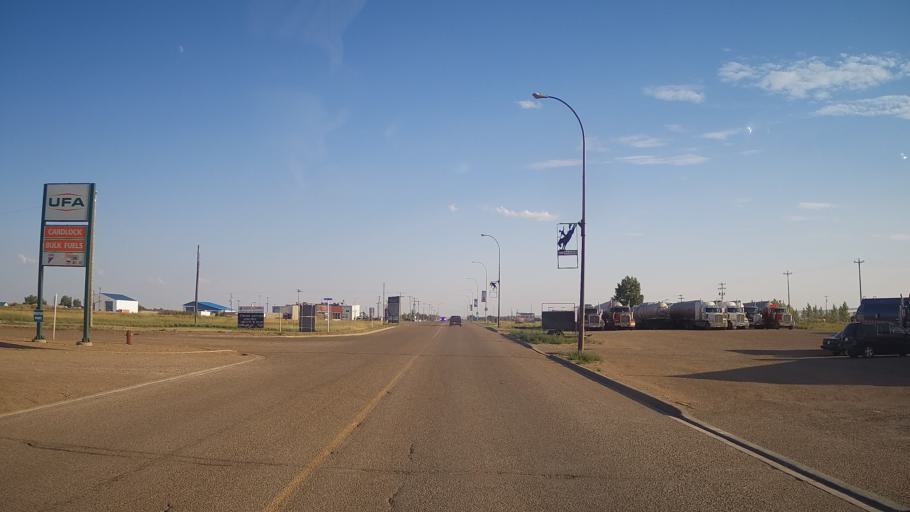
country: CA
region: Alberta
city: Hanna
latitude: 51.6389
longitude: -111.9422
